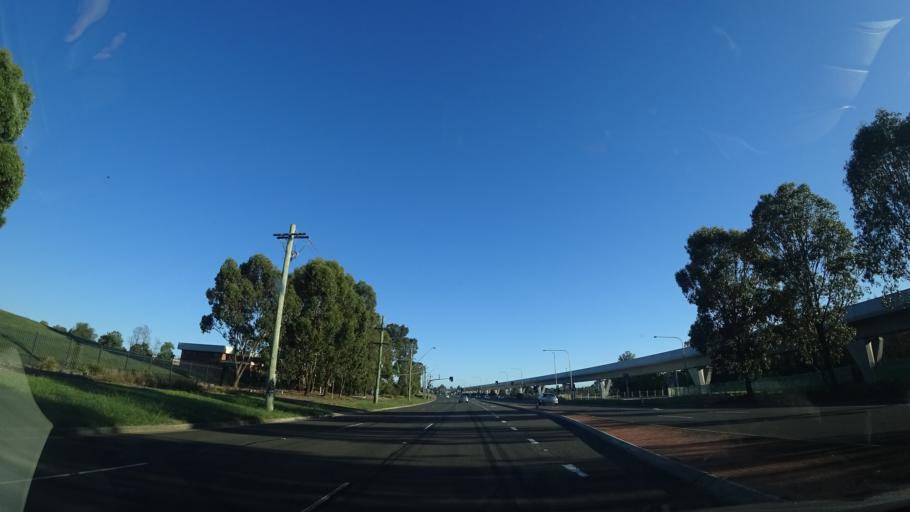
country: AU
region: New South Wales
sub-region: Blacktown
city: Stanhope Gardens
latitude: -33.7055
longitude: 150.9306
